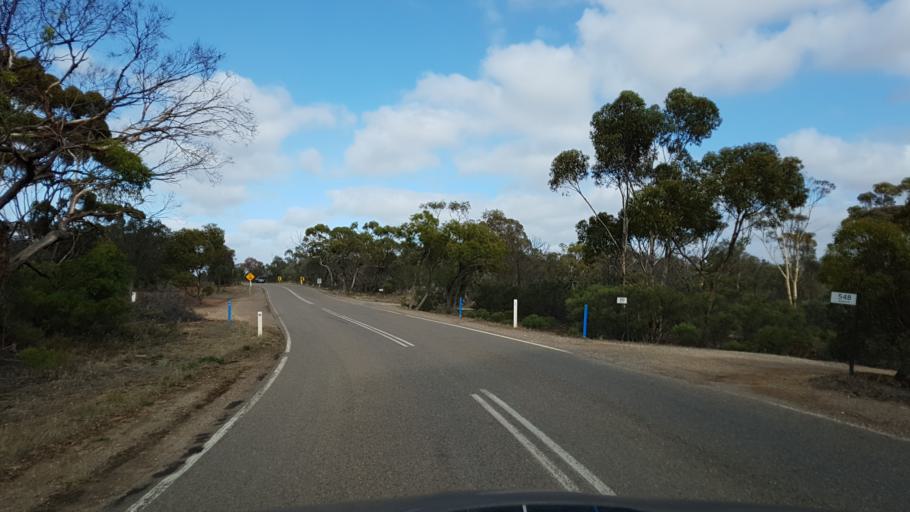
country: AU
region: South Australia
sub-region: Murray Bridge
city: Murray Bridge
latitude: -35.1121
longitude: 139.2237
